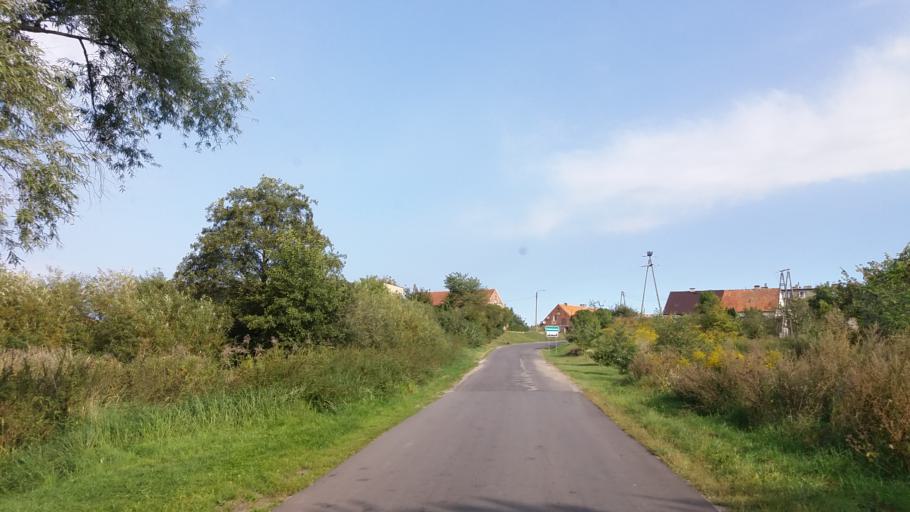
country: PL
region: West Pomeranian Voivodeship
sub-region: Powiat stargardzki
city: Suchan
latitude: 53.2256
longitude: 15.3417
